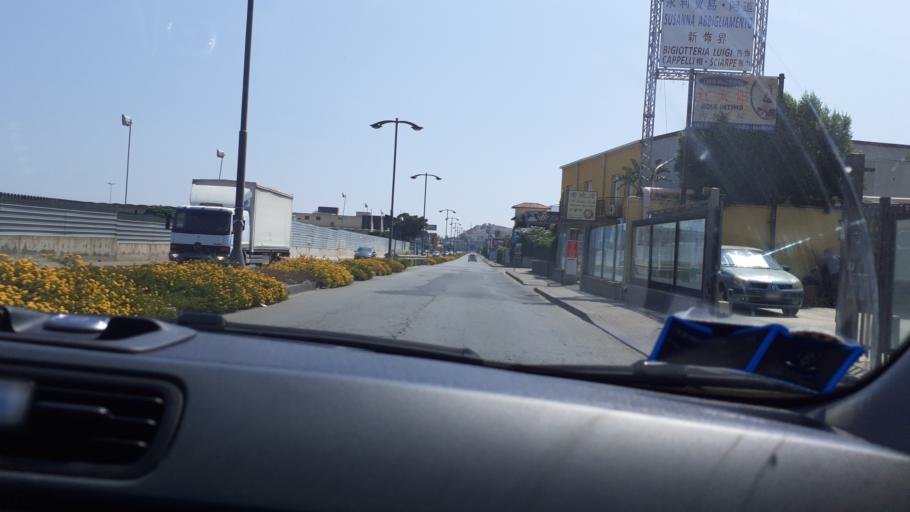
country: IT
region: Sicily
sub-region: Catania
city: Misterbianco
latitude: 37.5142
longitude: 15.0251
